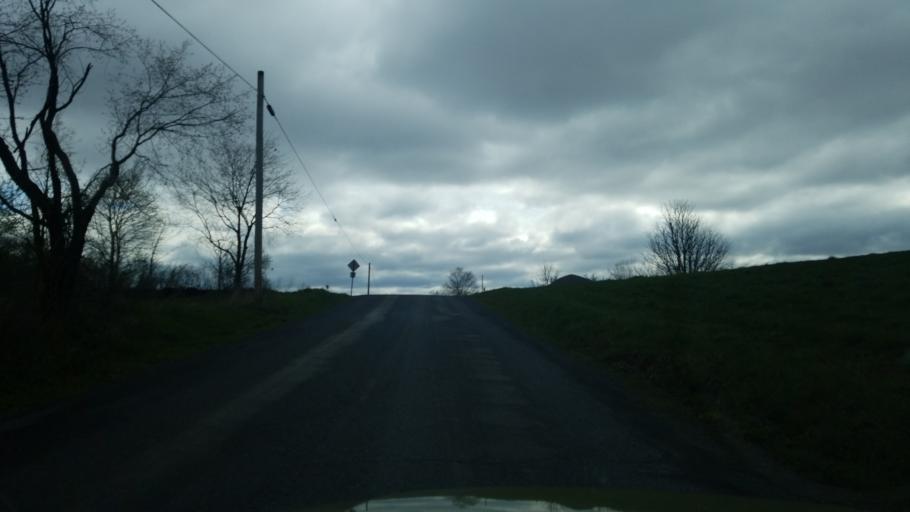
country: US
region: Pennsylvania
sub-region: Clearfield County
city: Clearfield
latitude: 41.0831
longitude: -78.4031
